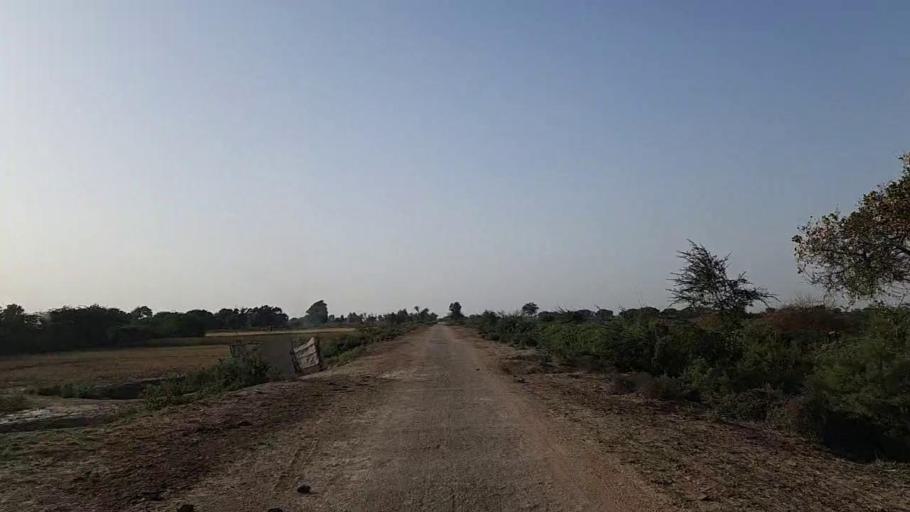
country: PK
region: Sindh
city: Jati
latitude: 24.3240
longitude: 68.1653
